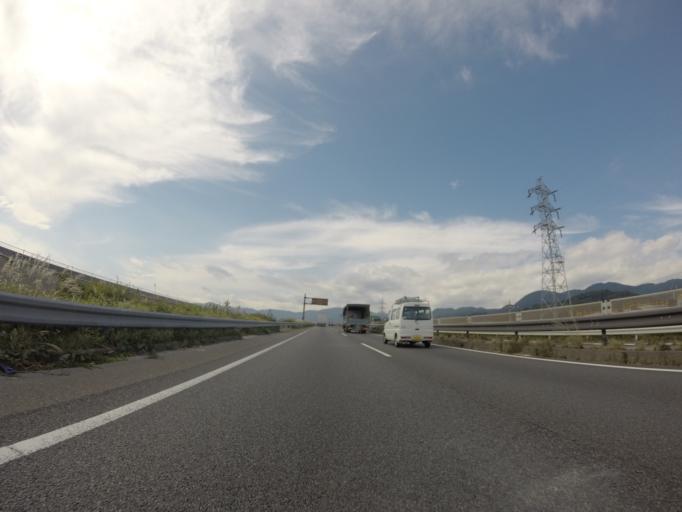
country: JP
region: Shizuoka
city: Fuji
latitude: 35.1157
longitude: 138.6154
